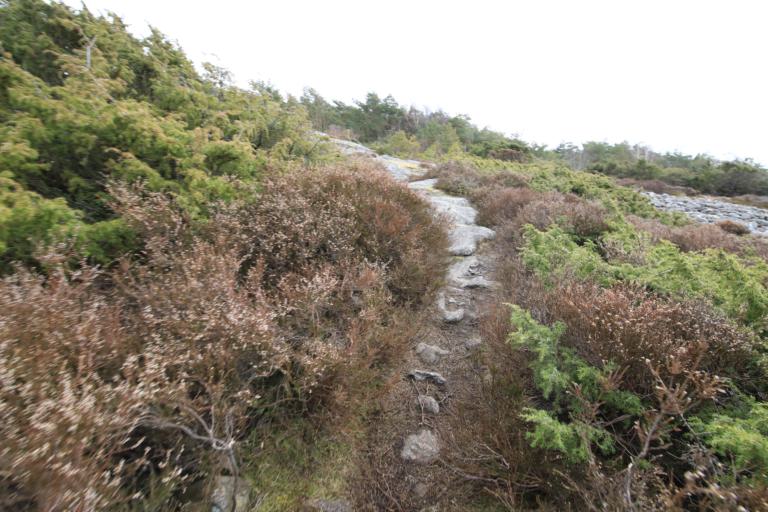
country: SE
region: Halland
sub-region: Kungsbacka Kommun
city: Frillesas
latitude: 57.2387
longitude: 12.1023
